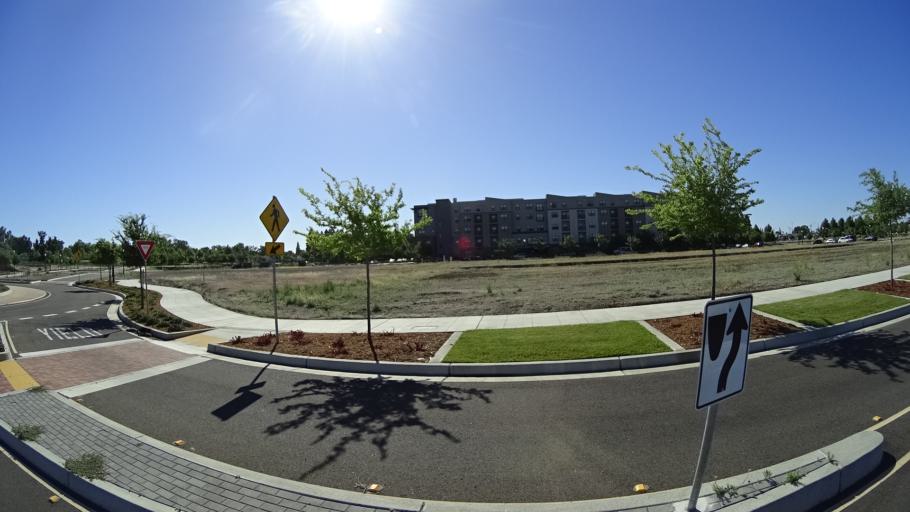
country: US
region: California
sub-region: Sacramento County
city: Sacramento
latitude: 38.5992
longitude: -121.4925
